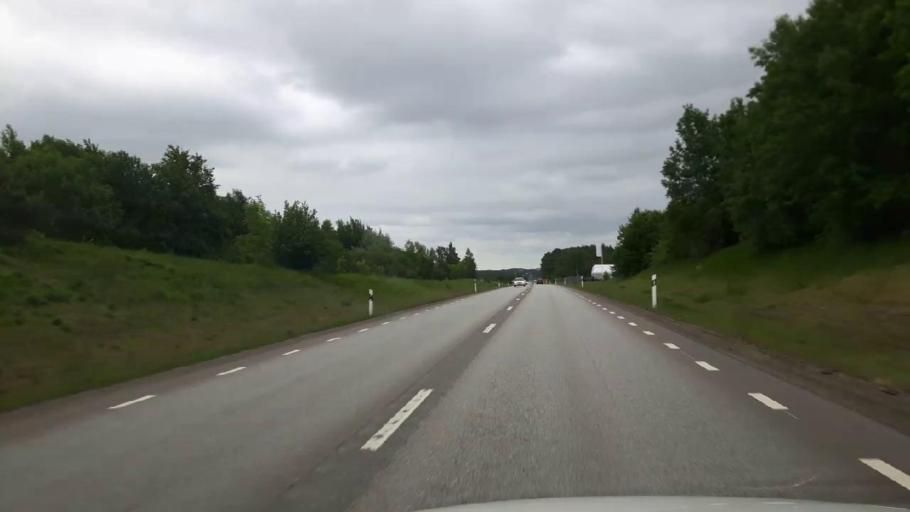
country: SE
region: Vaestmanland
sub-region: Kopings Kommun
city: Koping
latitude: 59.5415
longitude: 15.9373
